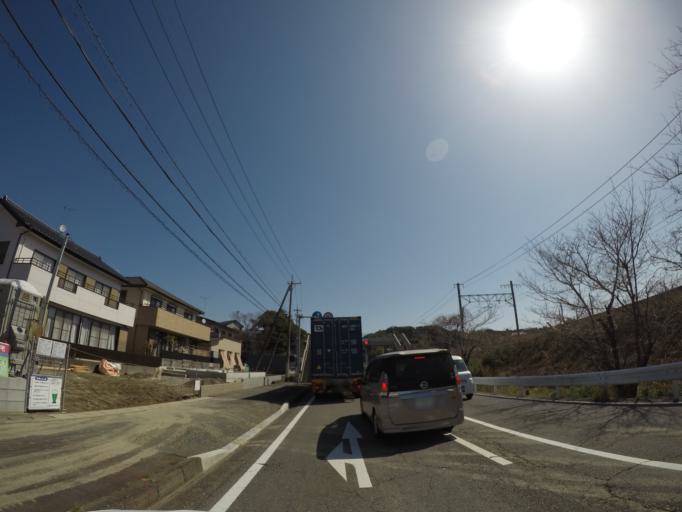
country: JP
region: Shizuoka
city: Kakegawa
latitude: 34.7608
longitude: 138.0770
